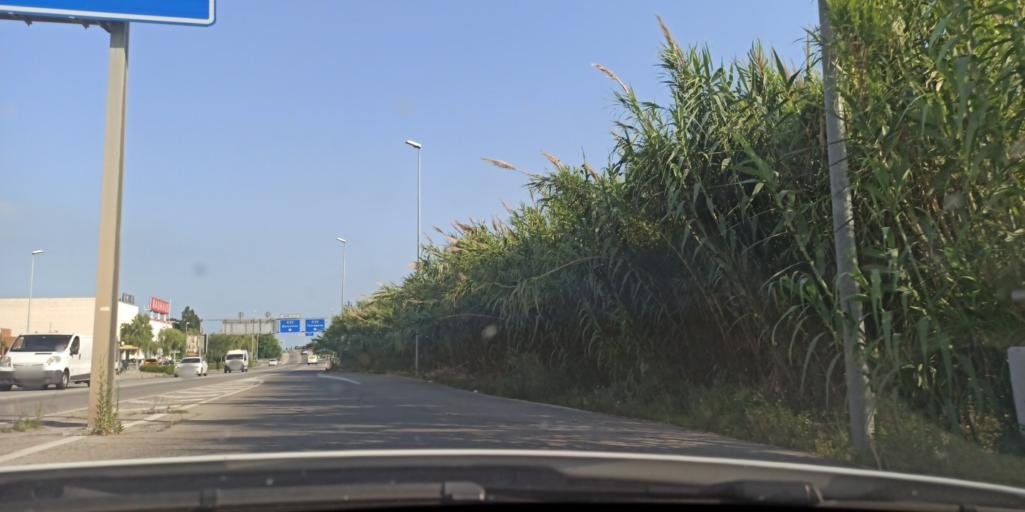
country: ES
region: Catalonia
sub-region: Provincia de Barcelona
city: Gava
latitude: 41.2955
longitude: 2.0063
